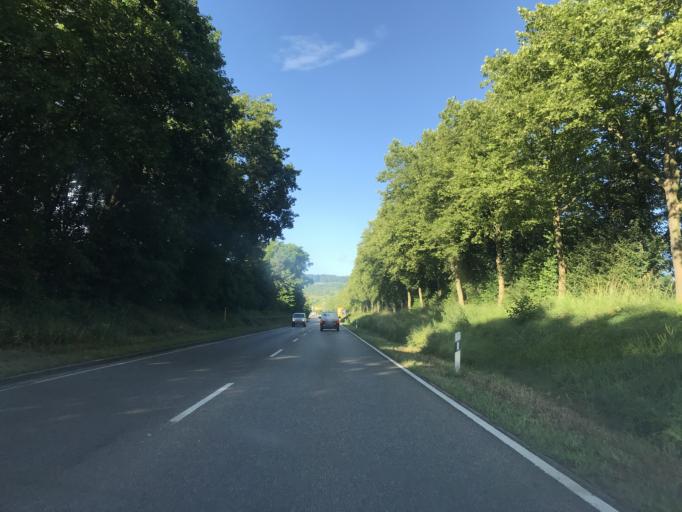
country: DE
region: Baden-Wuerttemberg
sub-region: Freiburg Region
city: Loerrach
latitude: 47.6292
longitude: 7.6645
